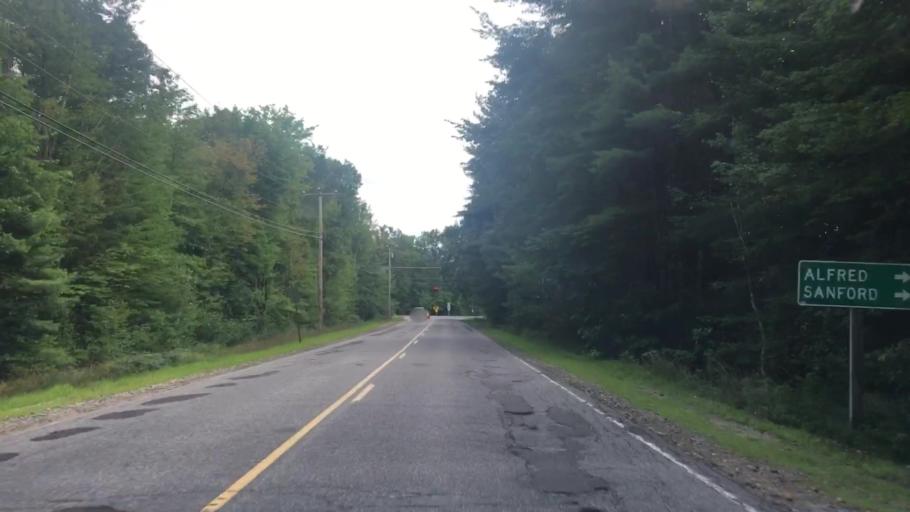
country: US
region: Maine
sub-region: York County
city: Waterboro
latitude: 43.5633
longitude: -70.7019
